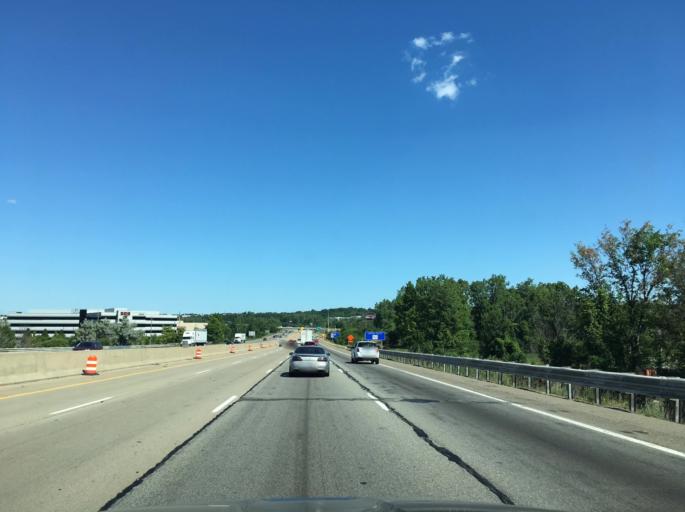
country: US
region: Michigan
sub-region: Oakland County
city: Auburn Hills
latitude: 42.6860
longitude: -83.2455
